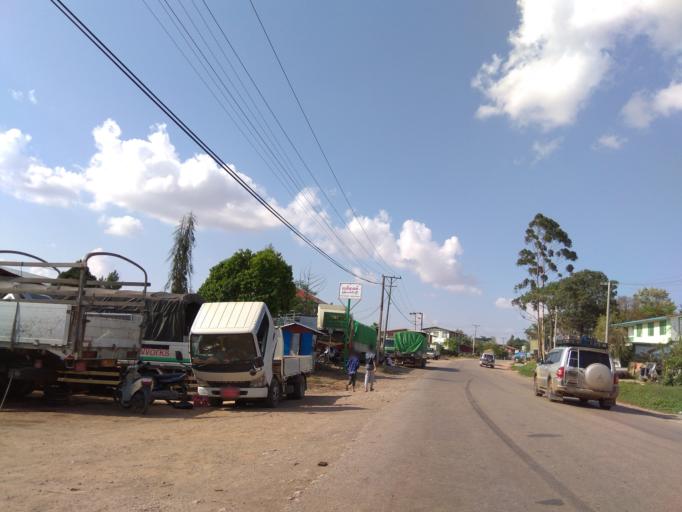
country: MM
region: Shan
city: Taunggyi
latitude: 20.6585
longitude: 96.6429
